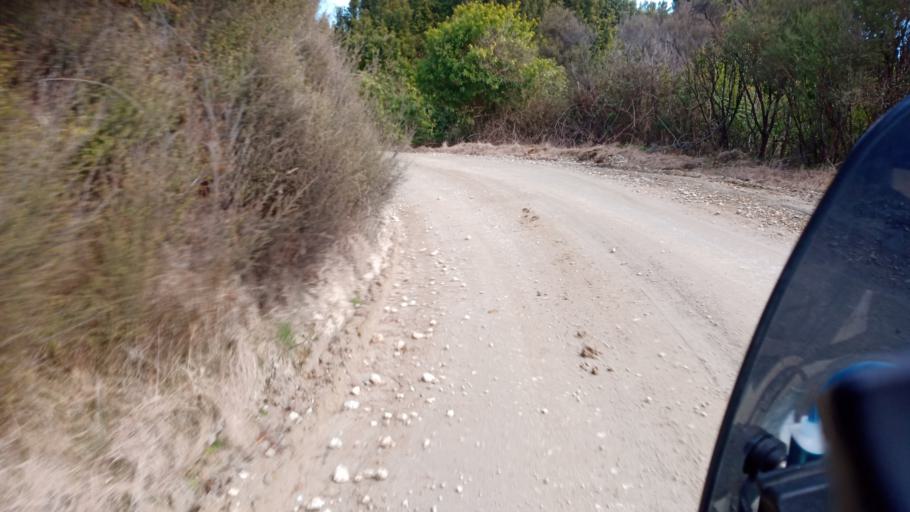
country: NZ
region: Gisborne
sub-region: Gisborne District
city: Gisborne
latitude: -38.8638
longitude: 177.7926
